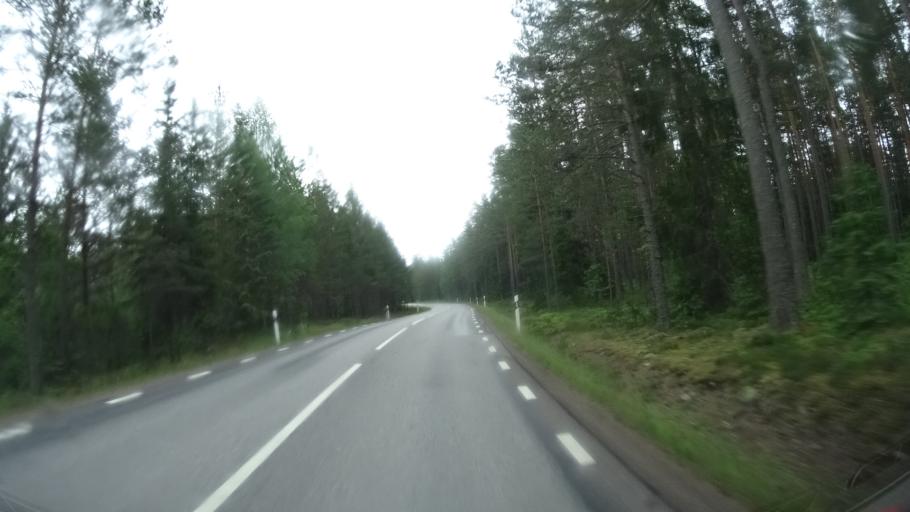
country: SE
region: Kalmar
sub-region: Hultsfreds Kommun
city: Hultsfred
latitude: 57.5286
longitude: 15.7868
